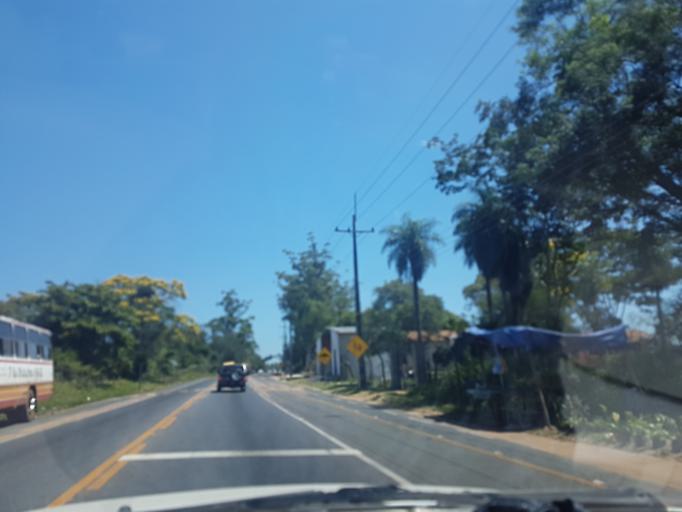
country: PY
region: Central
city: Aregua
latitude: -25.2287
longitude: -57.4180
